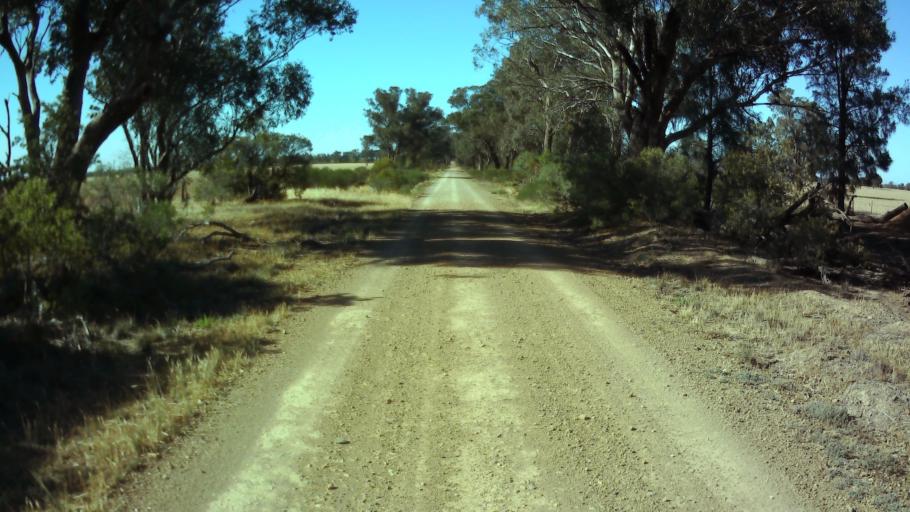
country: AU
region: New South Wales
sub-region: Weddin
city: Grenfell
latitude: -33.9166
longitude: 147.8756
